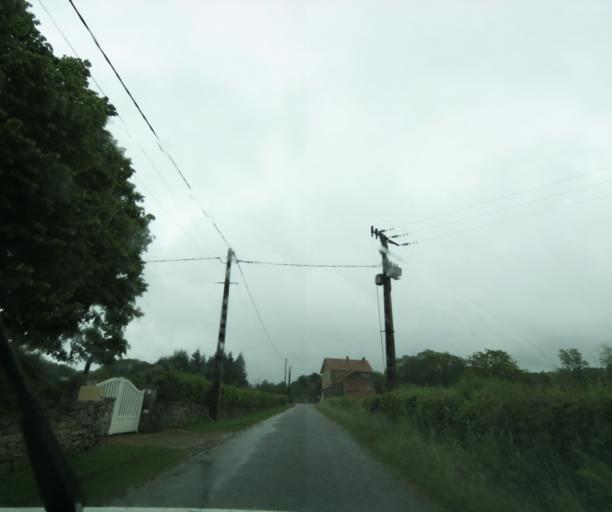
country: FR
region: Bourgogne
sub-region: Departement de Saone-et-Loire
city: Ciry-le-Noble
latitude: 46.5254
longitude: 4.3016
